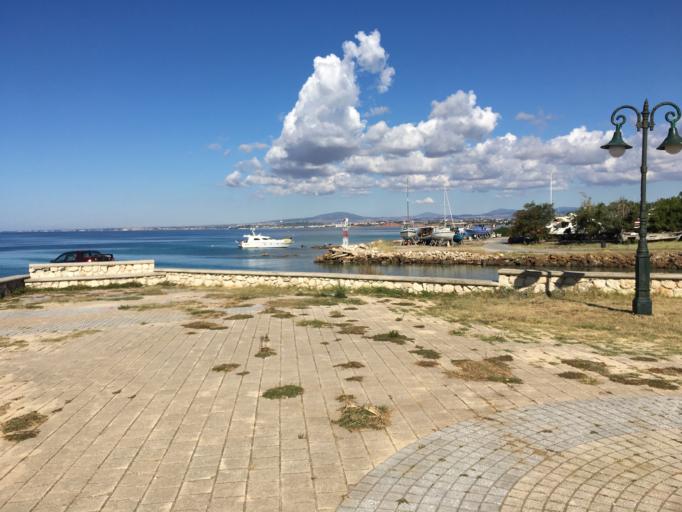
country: GR
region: Central Macedonia
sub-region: Nomos Chalkidikis
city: Nea Poteidaia
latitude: 40.1961
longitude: 23.3219
